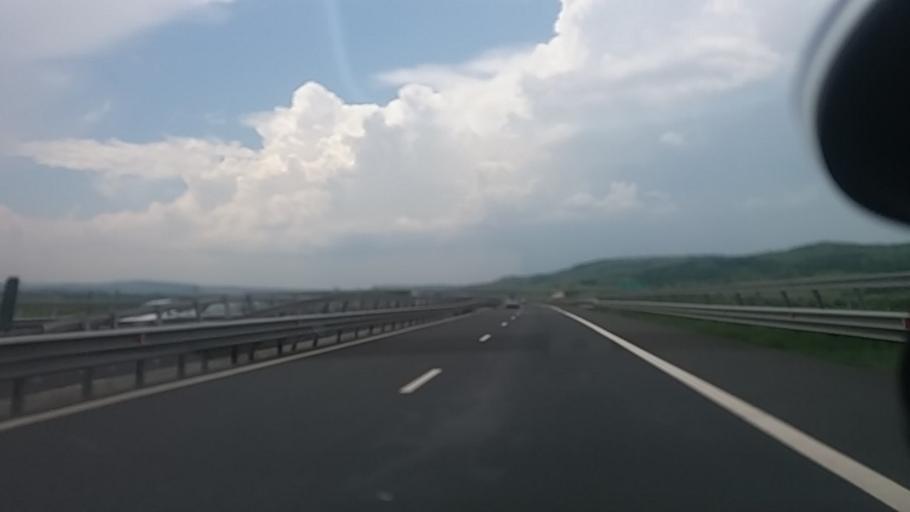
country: RO
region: Sibiu
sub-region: Comuna Apoldu de Jos
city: Apoldu de Jos
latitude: 45.8869
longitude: 23.8476
